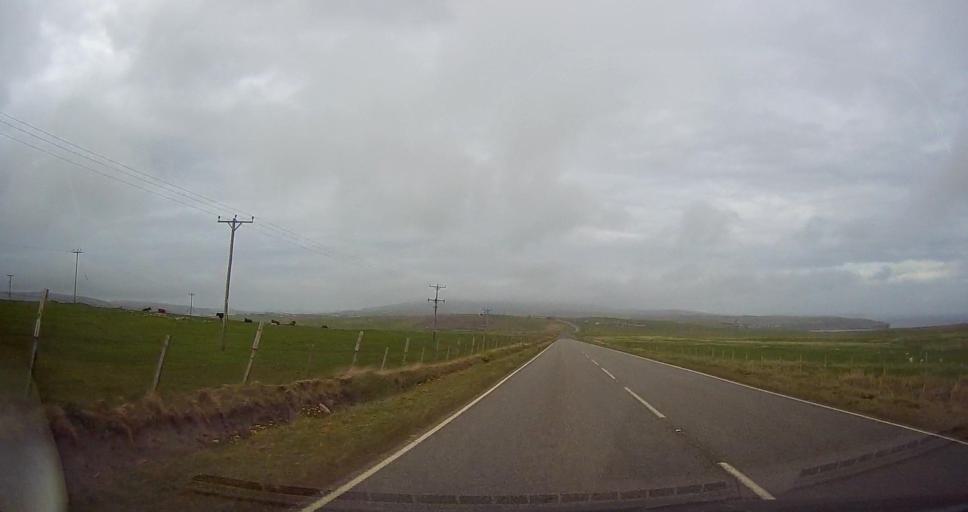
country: GB
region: Scotland
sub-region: Shetland Islands
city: Sandwick
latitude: 59.8988
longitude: -1.3035
